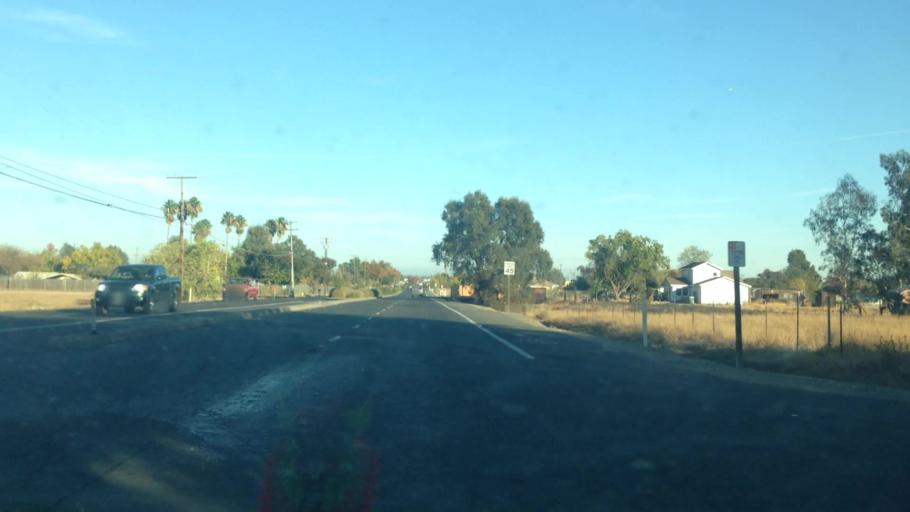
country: US
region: California
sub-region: Sacramento County
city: Rio Linda
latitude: 38.6906
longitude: -121.4153
